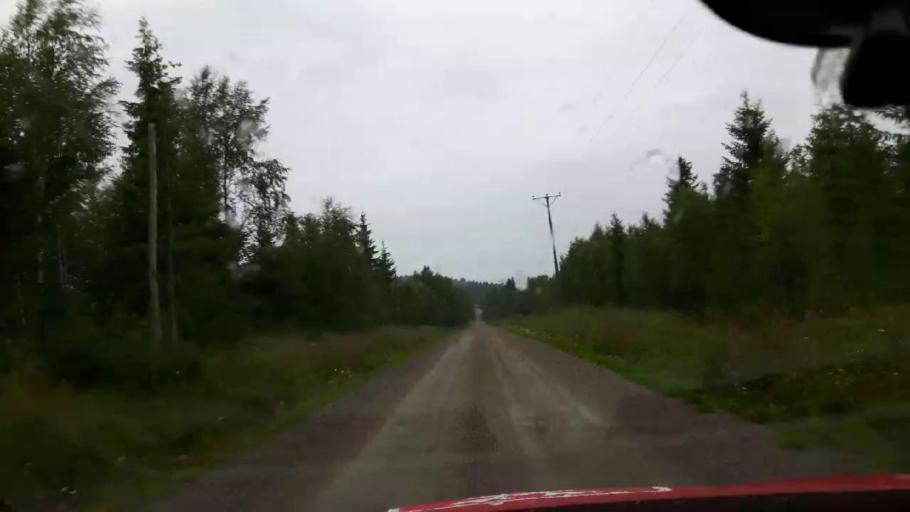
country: SE
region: Jaemtland
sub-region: OEstersunds Kommun
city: Brunflo
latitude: 62.7803
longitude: 14.9778
